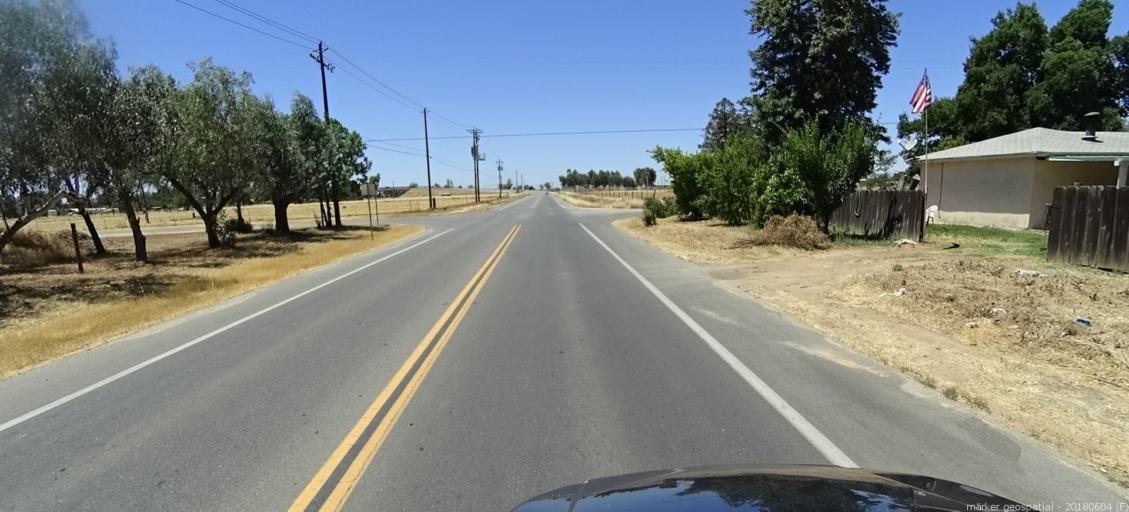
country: US
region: California
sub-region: Madera County
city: Madera
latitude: 36.9869
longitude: -120.0799
